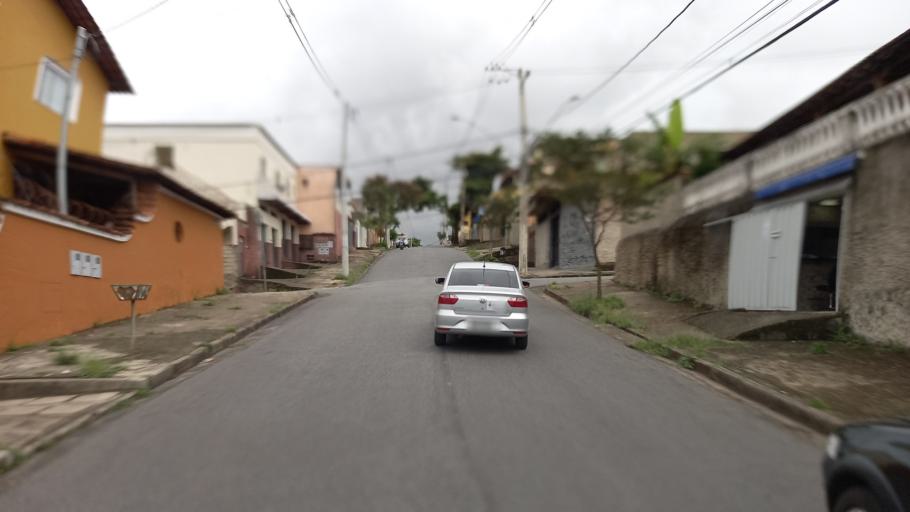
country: BR
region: Minas Gerais
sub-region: Belo Horizonte
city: Belo Horizonte
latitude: -19.8998
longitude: -43.8931
